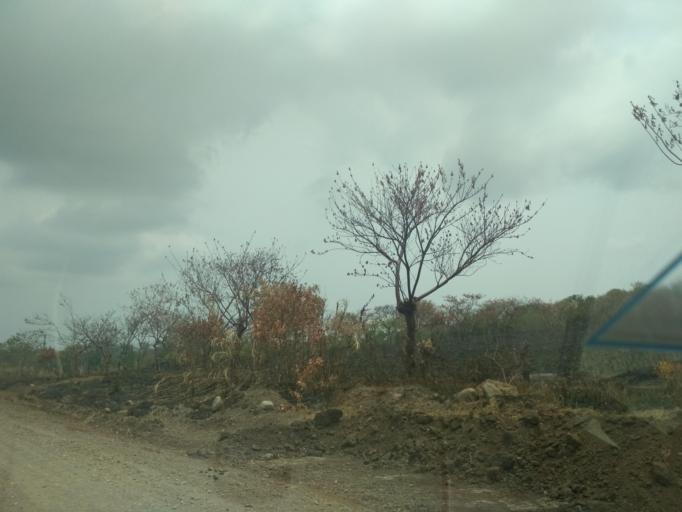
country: MX
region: Veracruz
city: Paso del Toro
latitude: 19.0077
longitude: -96.1326
